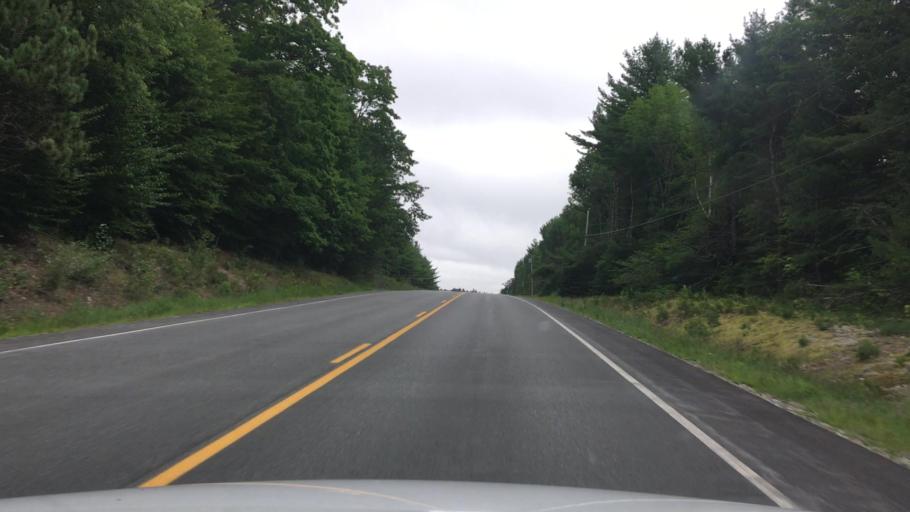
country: US
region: Maine
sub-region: Hancock County
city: Franklin
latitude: 44.8389
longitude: -68.1622
